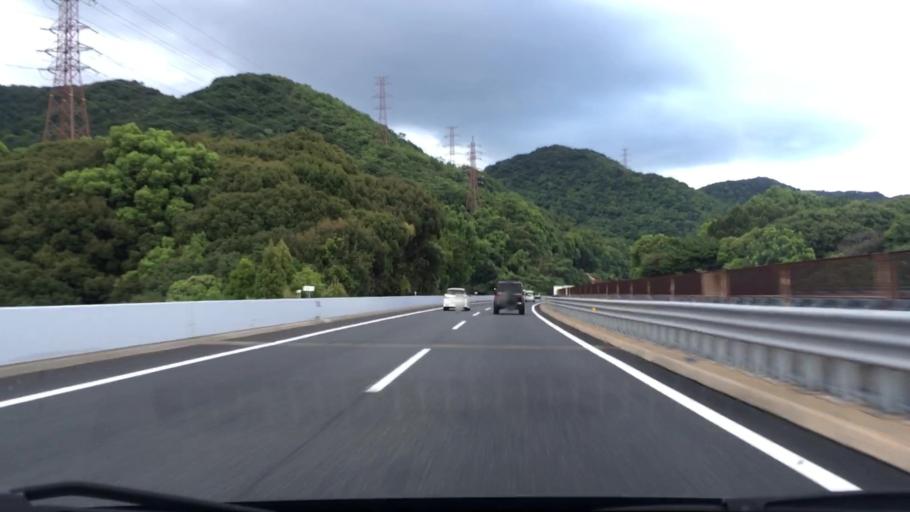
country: JP
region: Fukuoka
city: Kanda
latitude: 33.8582
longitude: 130.9393
